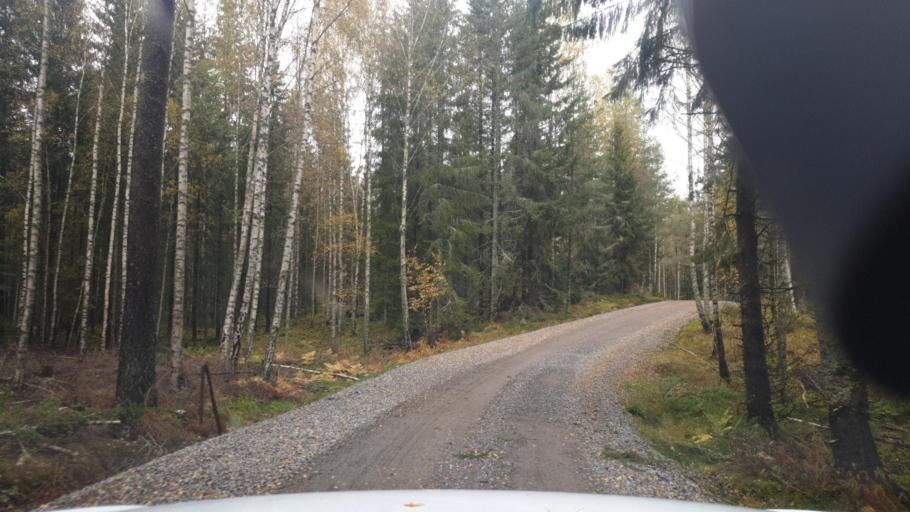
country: SE
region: Vaermland
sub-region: Karlstads Kommun
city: Edsvalla
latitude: 59.4584
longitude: 13.0987
